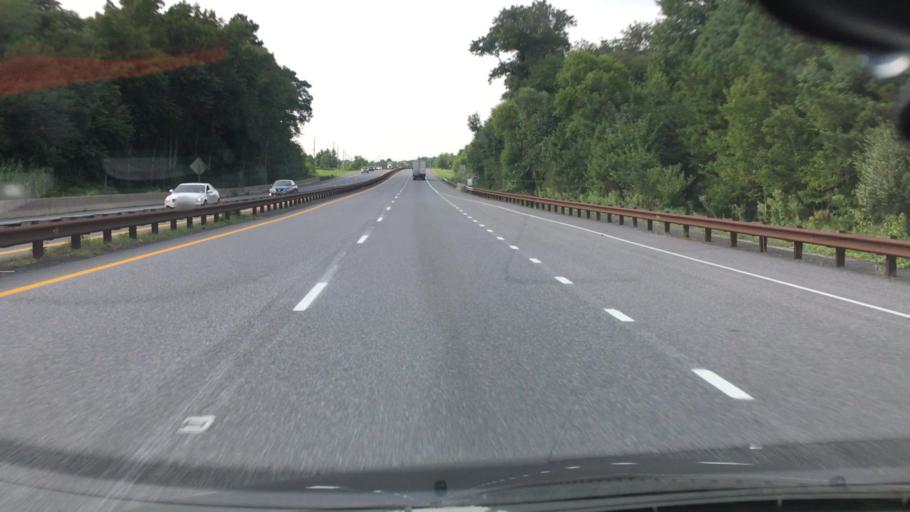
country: US
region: Delaware
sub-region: Sussex County
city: Selbyville
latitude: 38.4084
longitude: -75.2127
